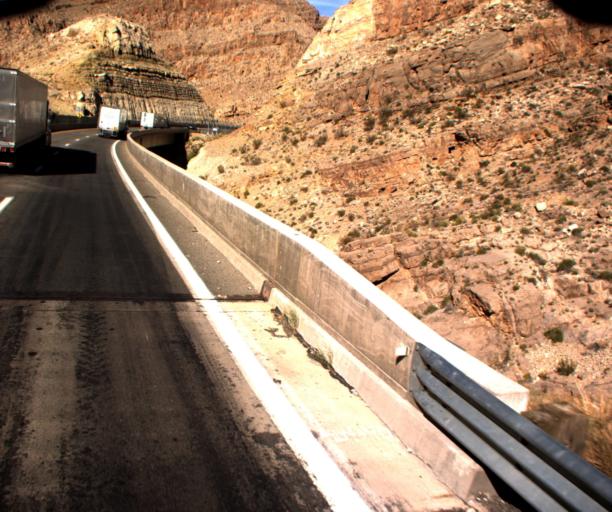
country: US
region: Arizona
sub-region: Mohave County
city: Beaver Dam
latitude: 36.9254
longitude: -113.8322
